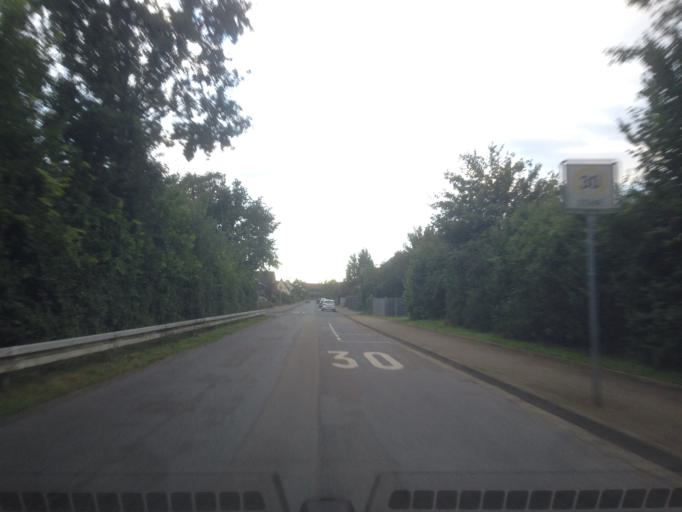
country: DE
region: North Rhine-Westphalia
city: Olfen
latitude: 51.7183
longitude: 7.3766
